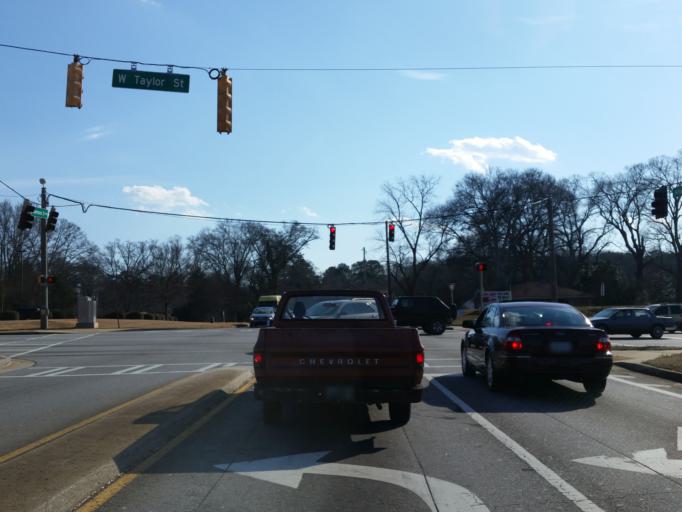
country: US
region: Georgia
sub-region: Spalding County
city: Experiment
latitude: 33.2477
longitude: -84.2867
